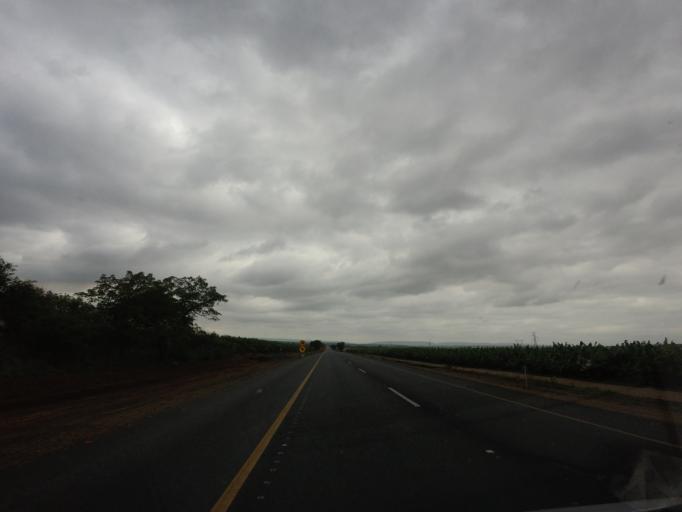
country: ZA
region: Mpumalanga
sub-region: Ehlanzeni District
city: Komatipoort
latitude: -25.4379
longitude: 31.7911
